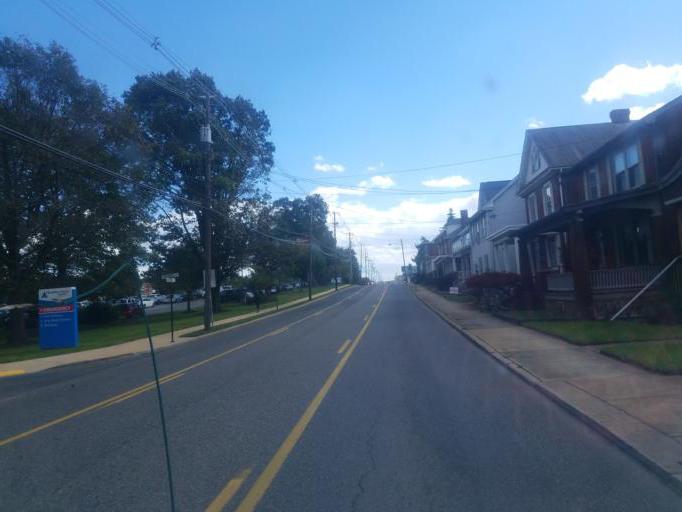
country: US
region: Pennsylvania
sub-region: Franklin County
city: Chambersburg
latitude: 39.9334
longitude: -77.6484
